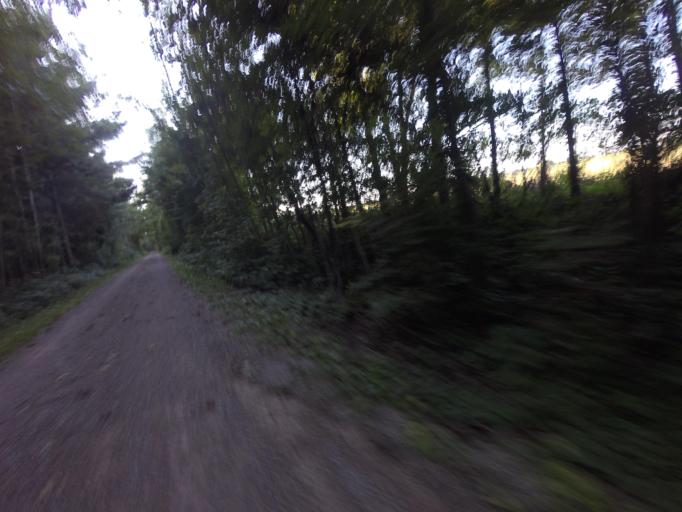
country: CA
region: Ontario
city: Goderich
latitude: 43.7584
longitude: -81.6871
